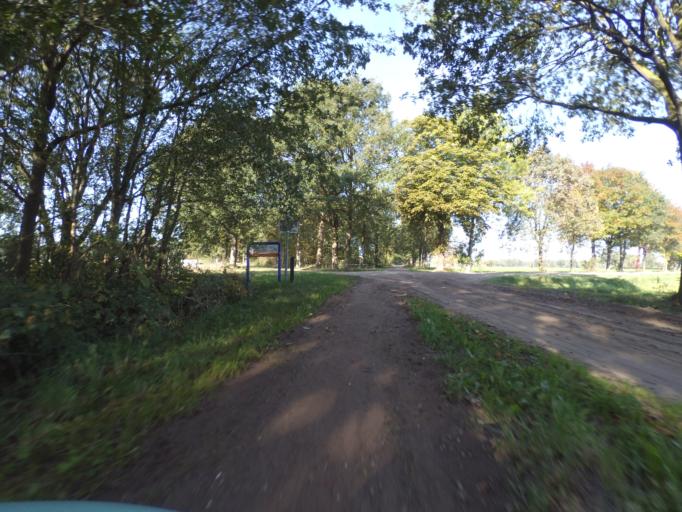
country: NL
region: Gelderland
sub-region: Gemeente Lochem
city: Barchem
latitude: 52.1036
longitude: 6.4378
